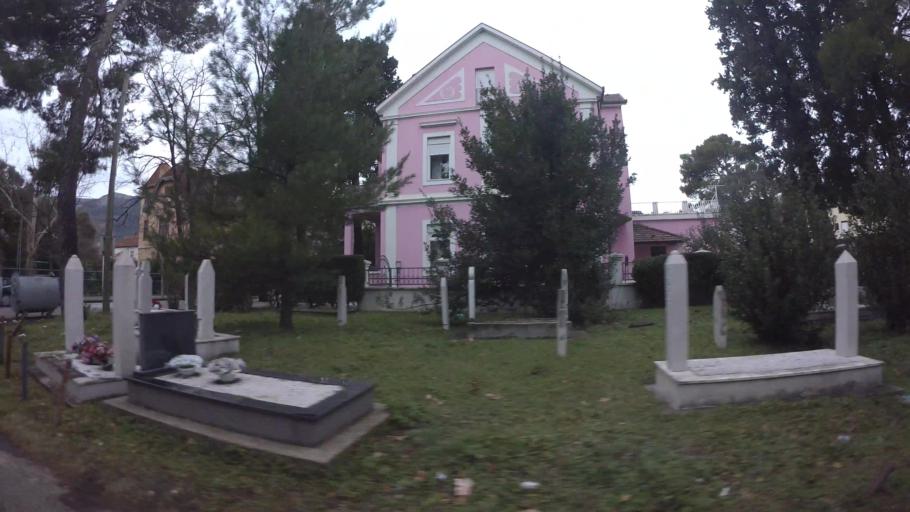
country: BA
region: Federation of Bosnia and Herzegovina
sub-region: Hercegovacko-Bosanski Kanton
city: Mostar
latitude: 43.3414
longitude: 17.8051
